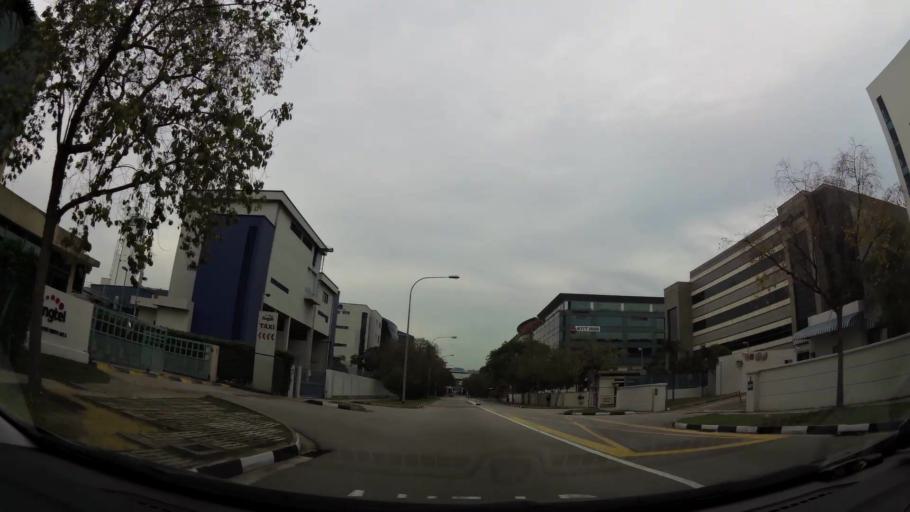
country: SG
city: Singapore
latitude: 1.3725
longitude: 103.8683
